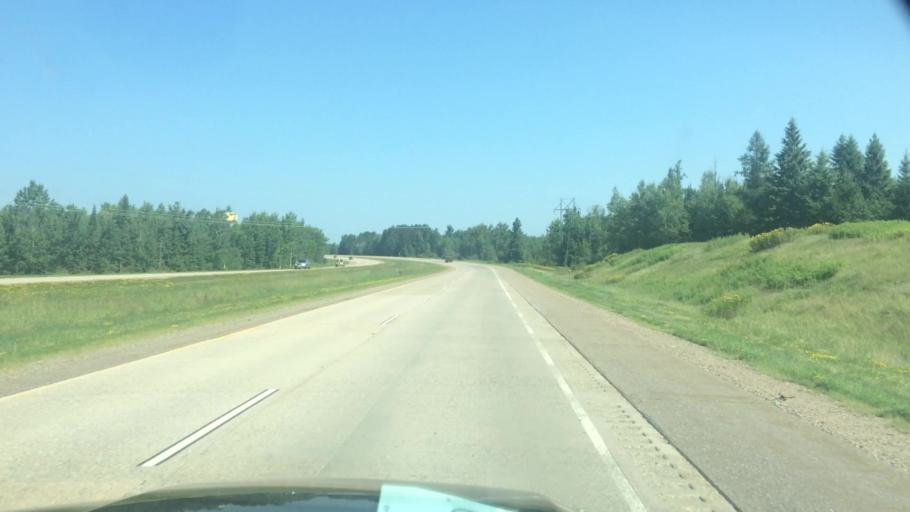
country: US
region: Wisconsin
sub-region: Lincoln County
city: Tomahawk
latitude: 45.3714
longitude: -89.6668
